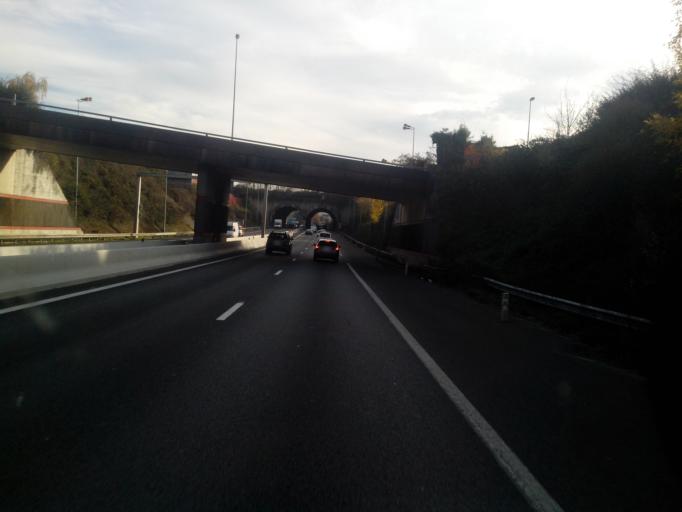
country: FR
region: Limousin
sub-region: Departement de la Haute-Vienne
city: Limoges
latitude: 45.8460
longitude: 1.2771
